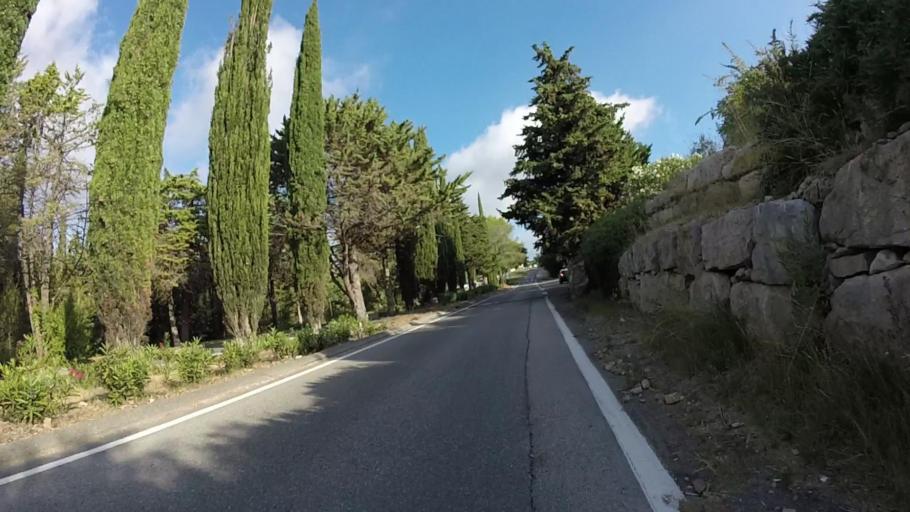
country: FR
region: Provence-Alpes-Cote d'Azur
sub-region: Departement des Alpes-Maritimes
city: Biot
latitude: 43.6212
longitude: 7.0637
